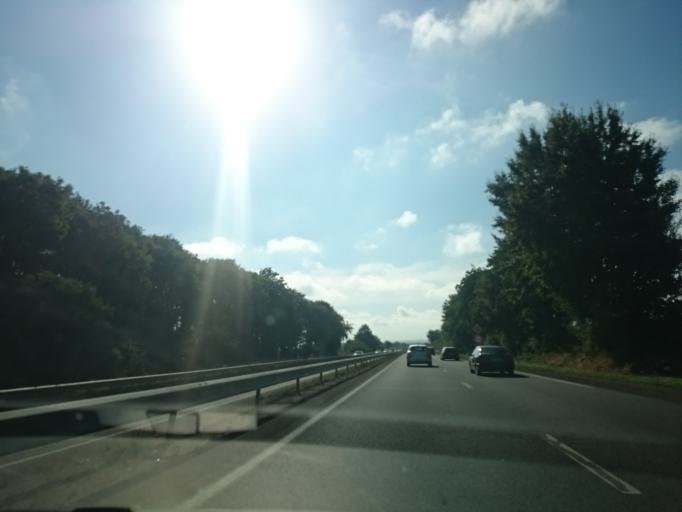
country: FR
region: Brittany
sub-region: Departement des Cotes-d'Armor
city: Plenee-Jugon
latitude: 48.3895
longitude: -2.3916
